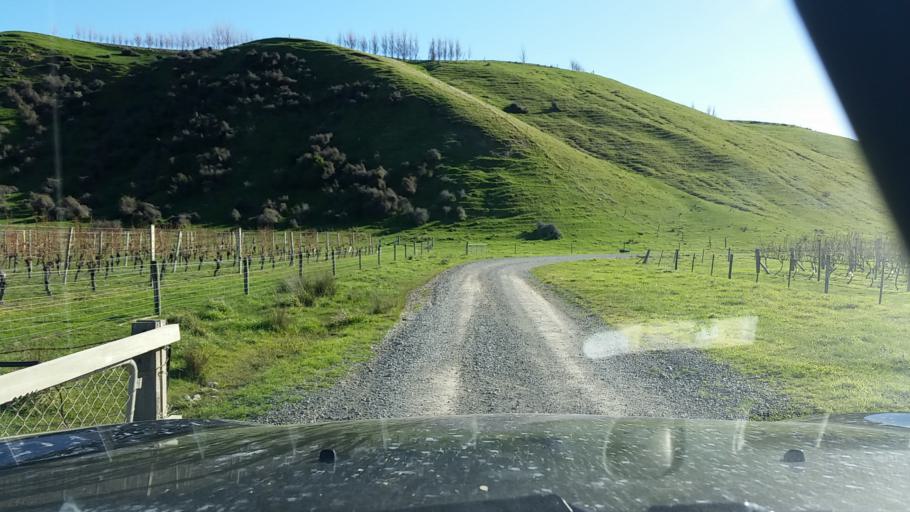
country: NZ
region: Marlborough
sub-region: Marlborough District
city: Blenheim
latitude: -41.6733
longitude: 174.1390
